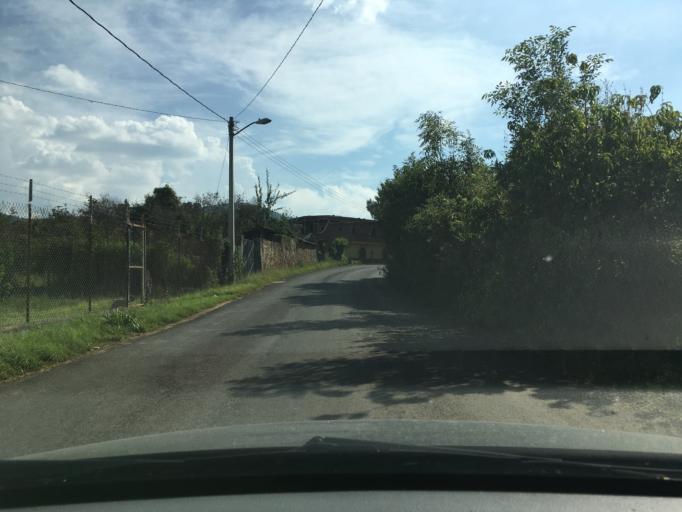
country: MX
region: Michoacan
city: Acuitzio del Canje
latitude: 19.5570
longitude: -101.2738
